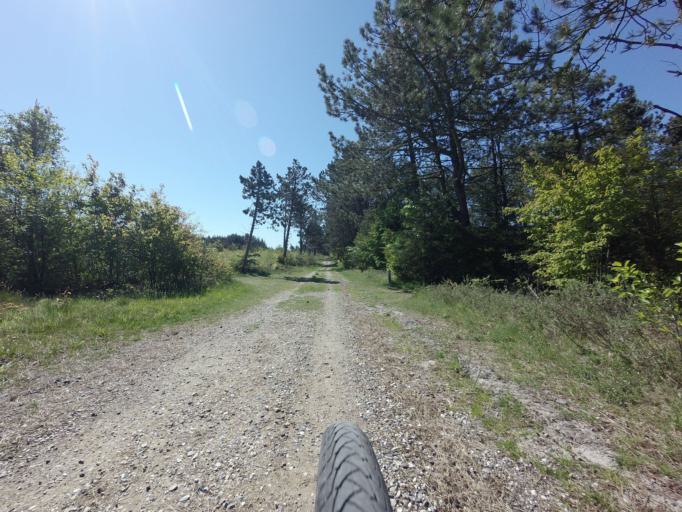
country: DK
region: North Denmark
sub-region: Jammerbugt Kommune
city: Pandrup
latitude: 57.2899
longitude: 9.6422
